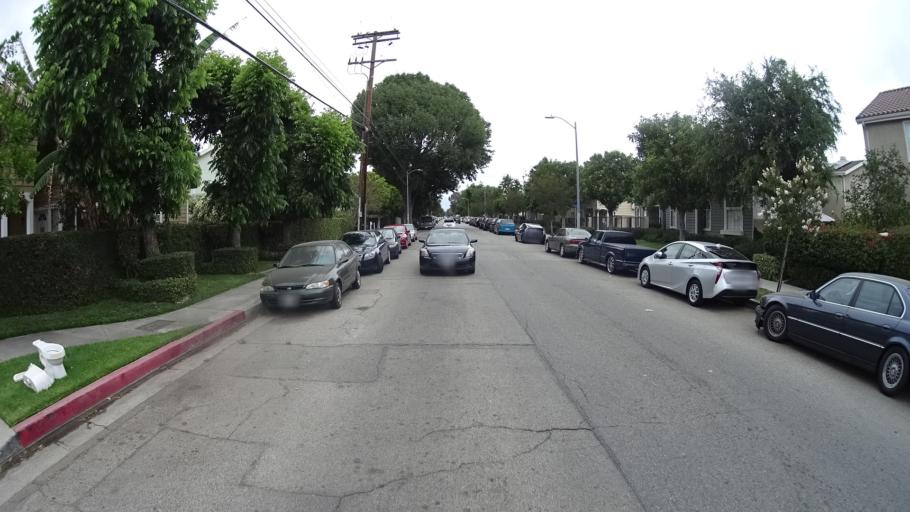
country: US
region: California
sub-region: Los Angeles County
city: San Fernando
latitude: 34.2370
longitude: -118.4610
